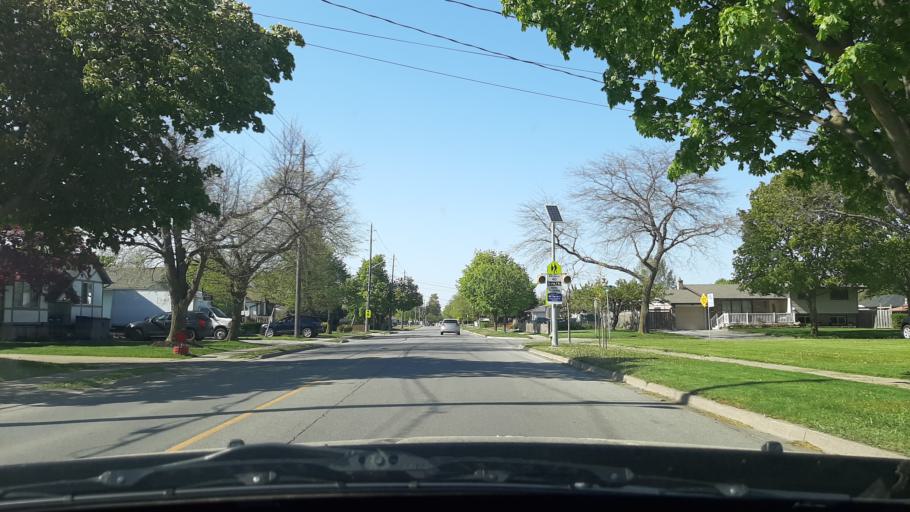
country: CA
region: Ontario
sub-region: Regional Municipality of Niagara
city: St. Catharines
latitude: 43.1971
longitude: -79.2112
